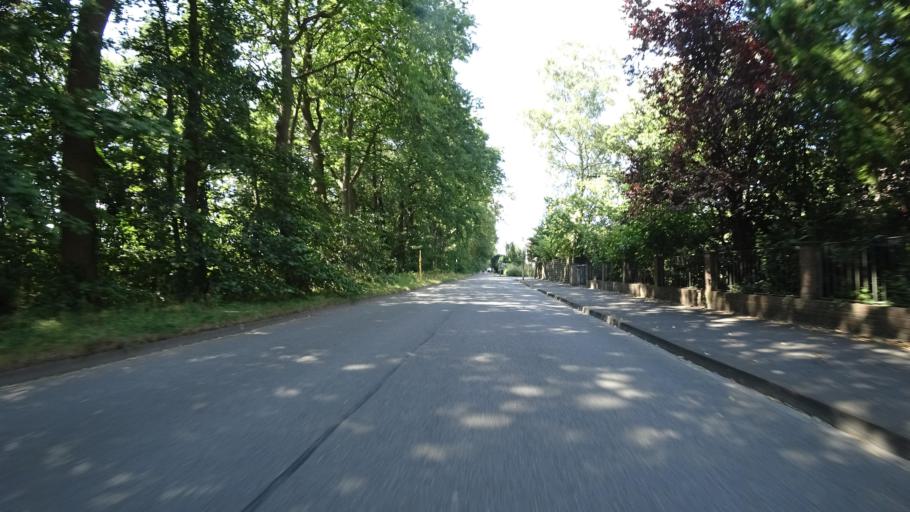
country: DE
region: North Rhine-Westphalia
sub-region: Regierungsbezirk Detmold
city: Guetersloh
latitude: 51.9239
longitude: 8.3925
